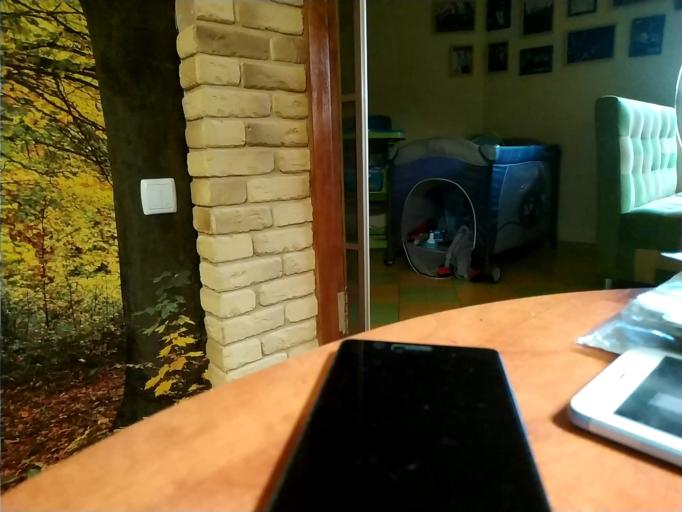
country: RU
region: Orjol
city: Znamenskoye
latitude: 53.5733
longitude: 35.4795
